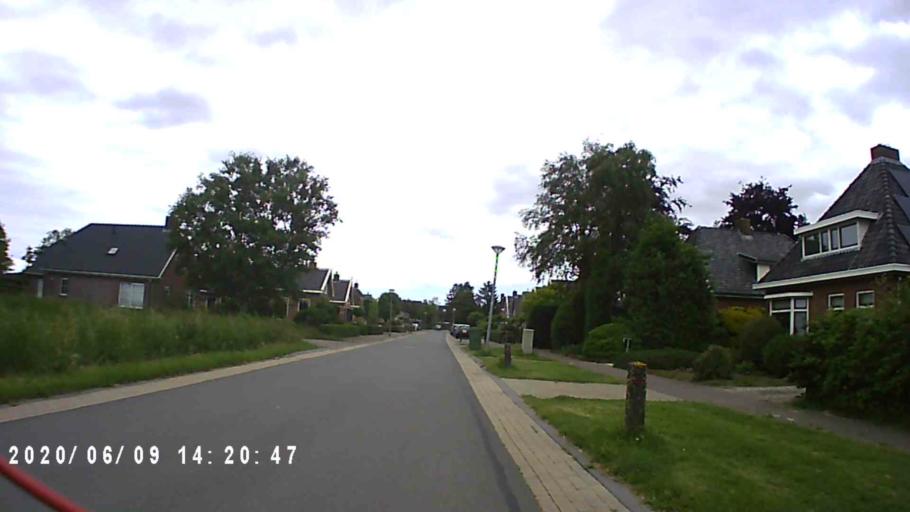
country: NL
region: Groningen
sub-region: Gemeente Bedum
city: Bedum
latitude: 53.2954
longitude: 6.5923
